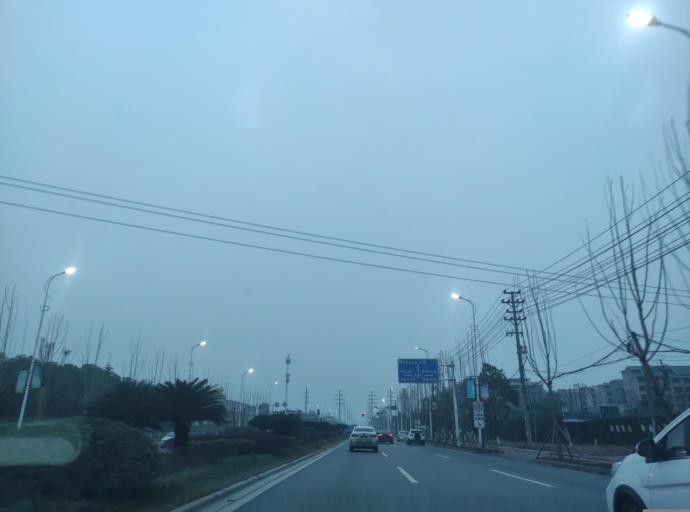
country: CN
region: Jiangxi Sheng
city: Pingxiang
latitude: 27.6683
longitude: 113.8733
